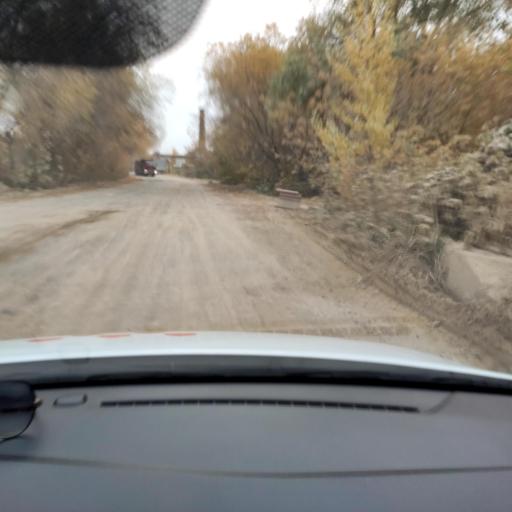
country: RU
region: Tatarstan
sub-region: Gorod Kazan'
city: Kazan
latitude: 55.7442
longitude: 49.0983
